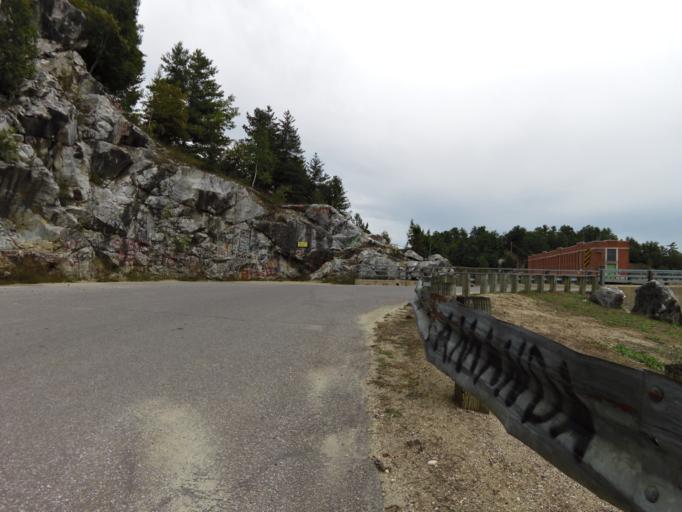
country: CA
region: Quebec
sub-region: Outaouais
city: Wakefield
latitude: 45.8110
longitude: -75.9334
